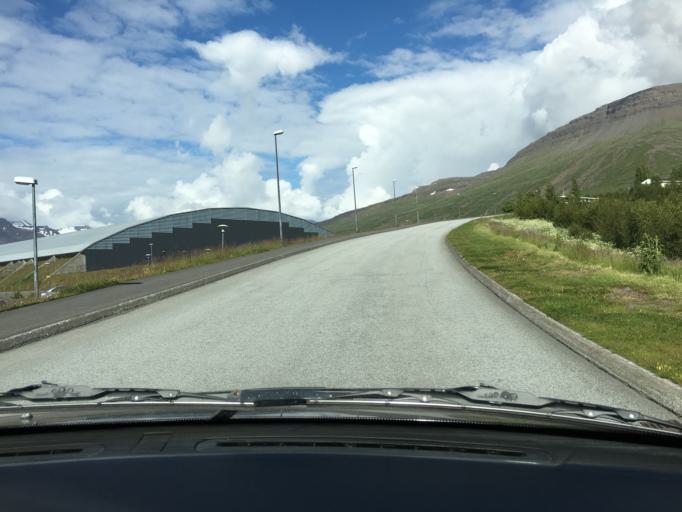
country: IS
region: East
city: Reydarfjoerdur
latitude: 65.0338
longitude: -14.2066
